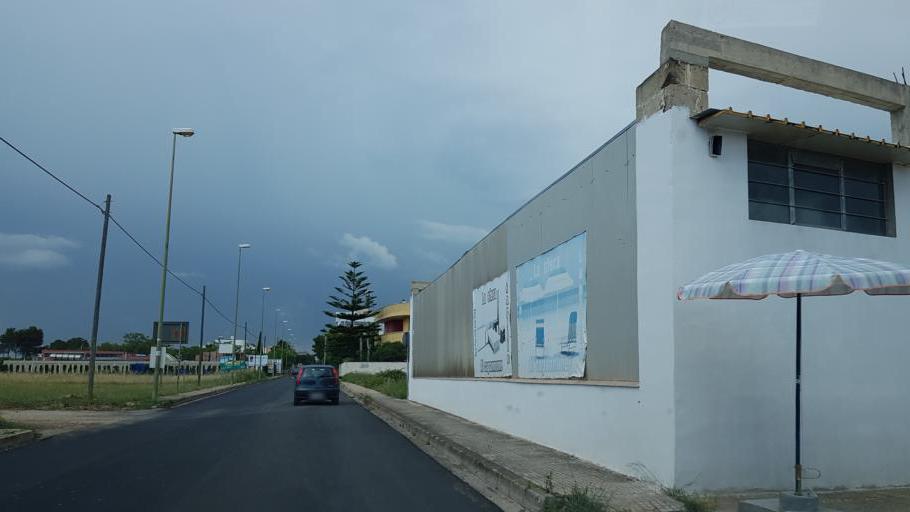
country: IT
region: Apulia
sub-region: Provincia di Lecce
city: Porto Cesareo
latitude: 40.2918
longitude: 17.8536
